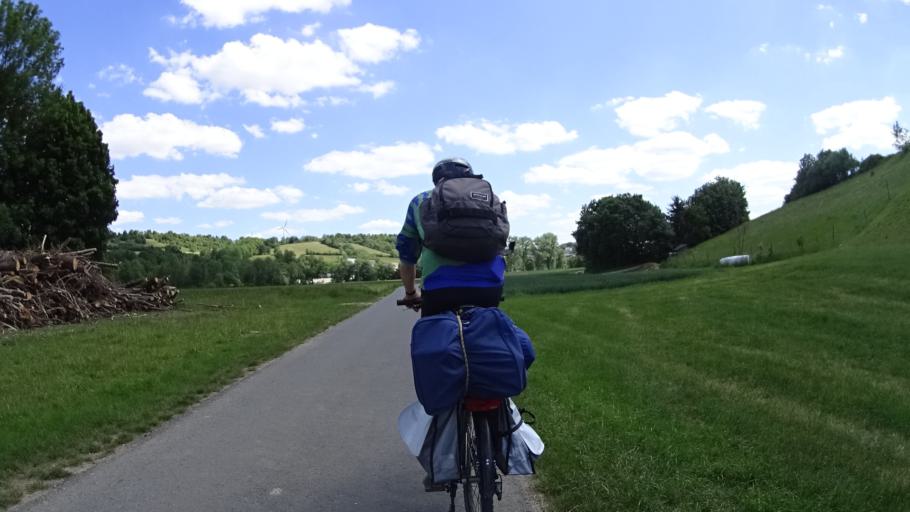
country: DE
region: Bavaria
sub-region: Regierungsbezirk Unterfranken
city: Bieberehren
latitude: 49.5187
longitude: 9.9951
